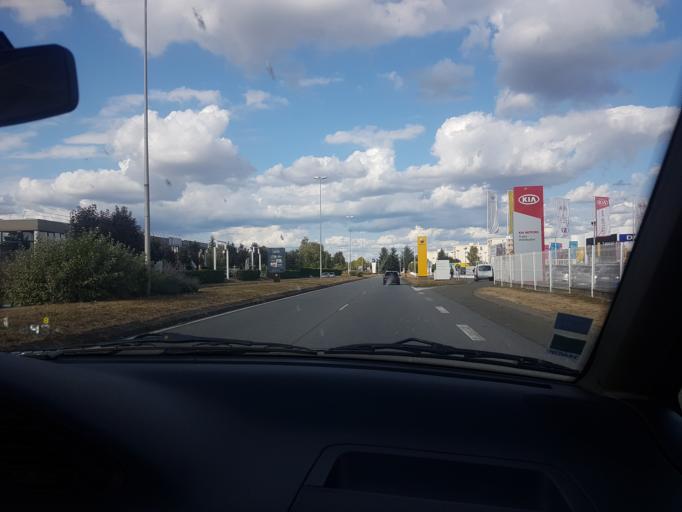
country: FR
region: Ile-de-France
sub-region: Departement des Yvelines
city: Maurepas
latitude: 48.7576
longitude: 1.9319
